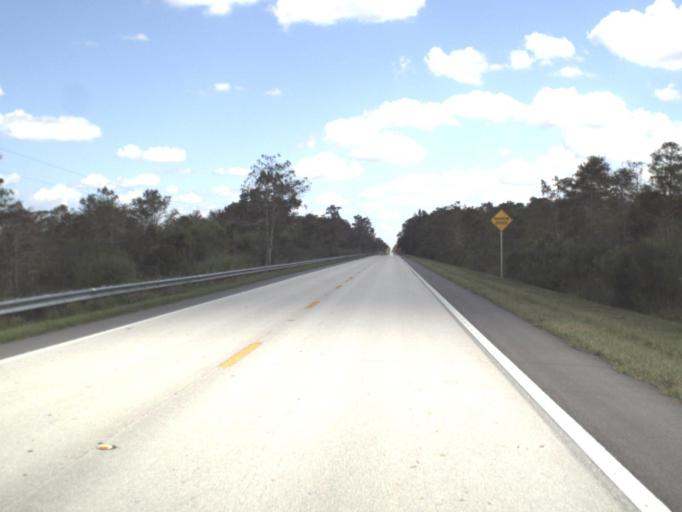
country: US
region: Florida
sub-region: Miami-Dade County
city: Kendall West
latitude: 25.8585
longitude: -81.0495
